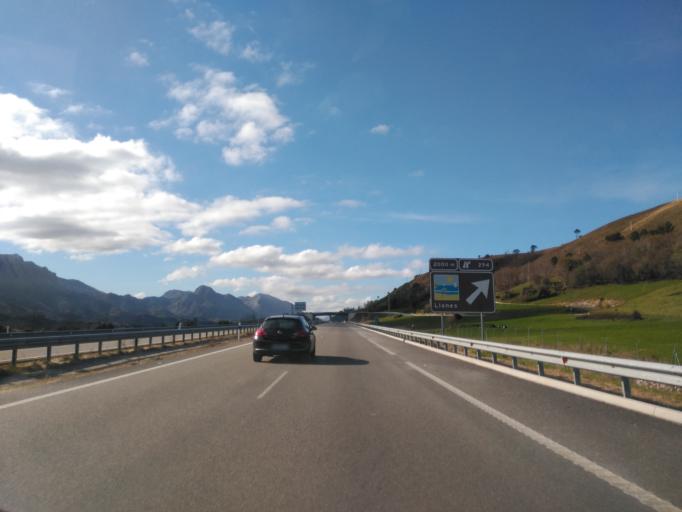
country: ES
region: Asturias
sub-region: Province of Asturias
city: Llanes
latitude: 43.4029
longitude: -4.7308
